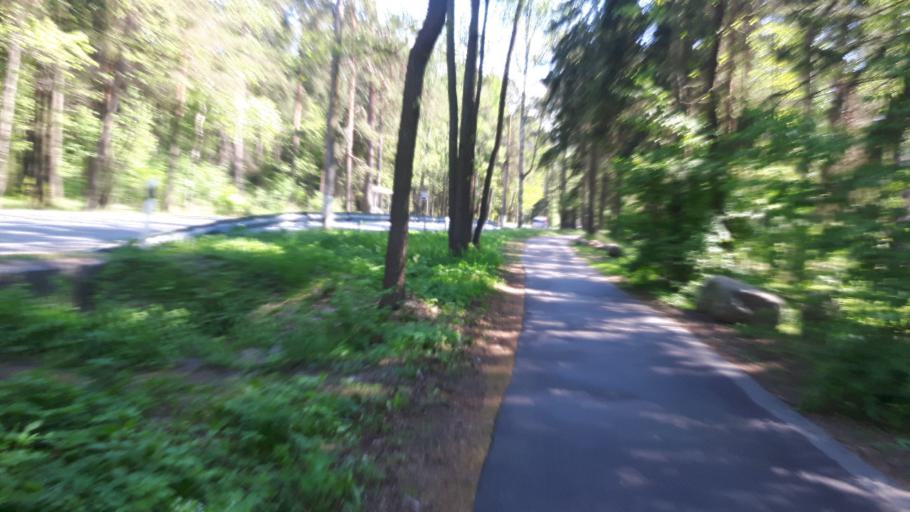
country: RU
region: St.-Petersburg
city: Komarovo
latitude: 60.1721
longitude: 29.8087
